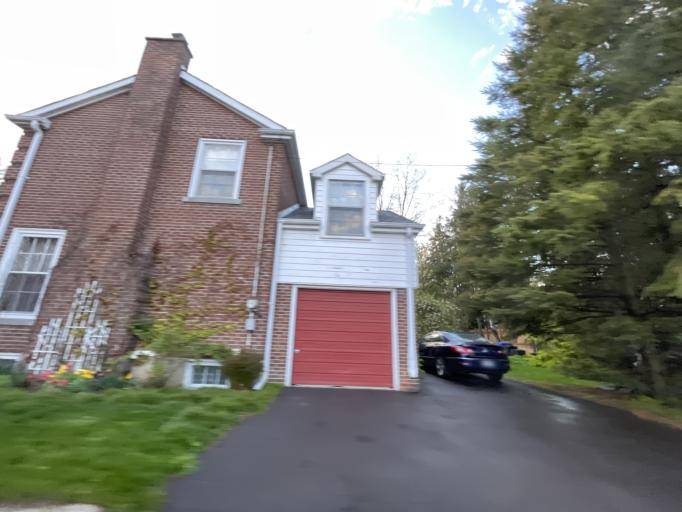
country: CA
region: Ontario
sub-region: Wellington County
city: Guelph
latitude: 43.5501
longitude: -80.2419
